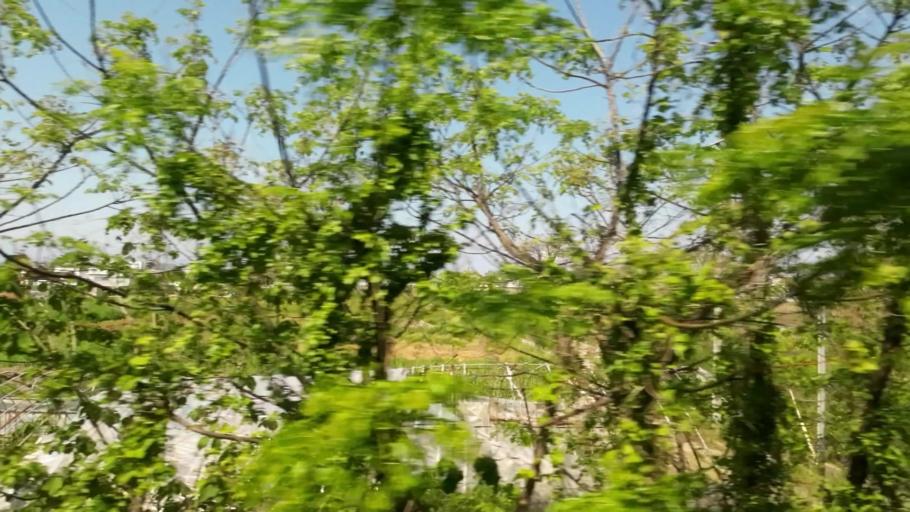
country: JP
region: Kagawa
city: Kan'onjicho
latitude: 34.1159
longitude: 133.6479
